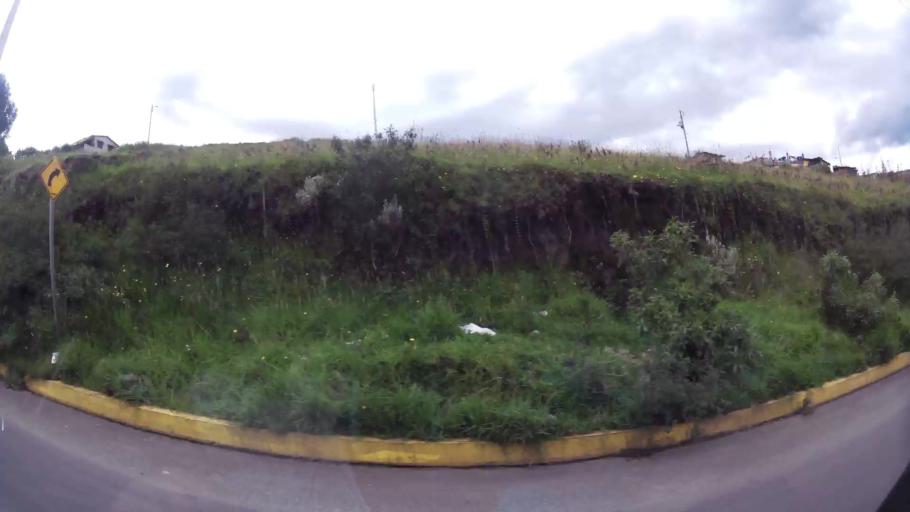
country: EC
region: Pichincha
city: Sangolqui
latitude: -0.3281
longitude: -78.5251
